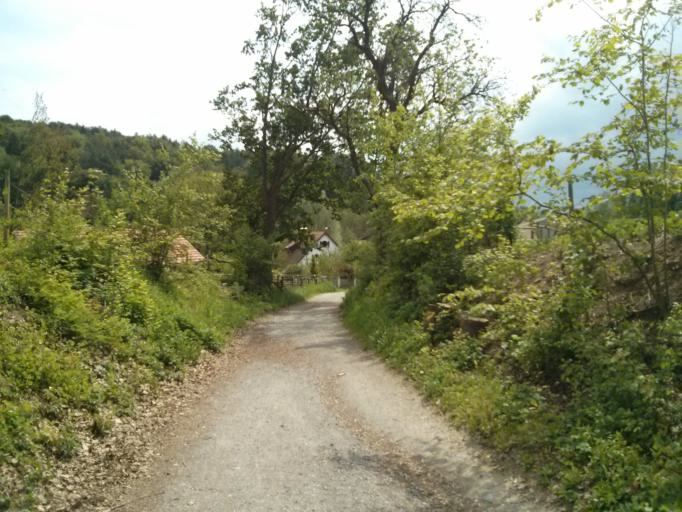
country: AT
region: Styria
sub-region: Politischer Bezirk Graz-Umgebung
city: Stattegg
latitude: 47.1350
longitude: 15.4243
